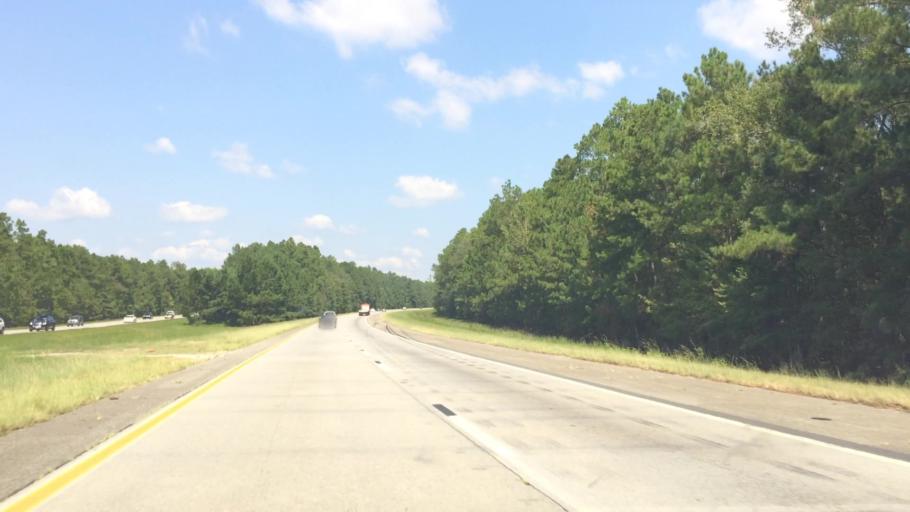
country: US
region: South Carolina
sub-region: Colleton County
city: Walterboro
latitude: 33.0388
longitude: -80.6689
